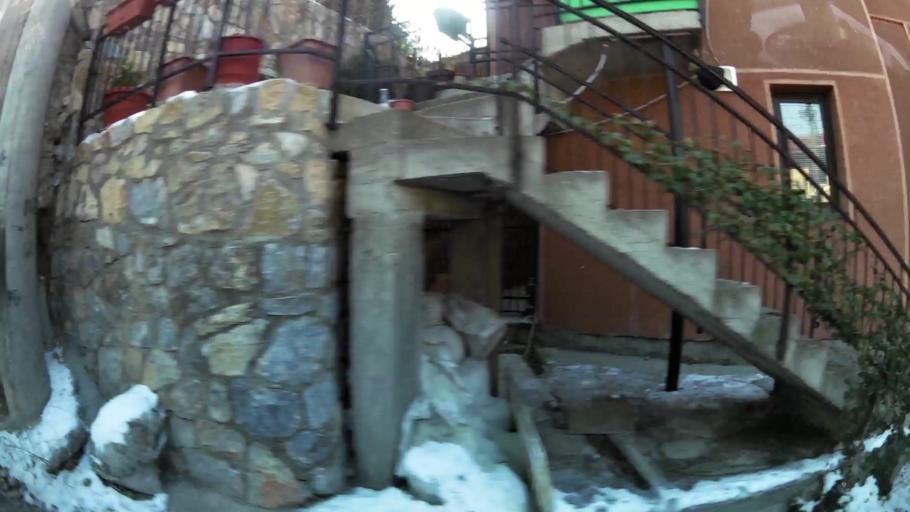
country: MK
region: Karpos
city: Skopje
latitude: 41.9829
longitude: 21.4243
